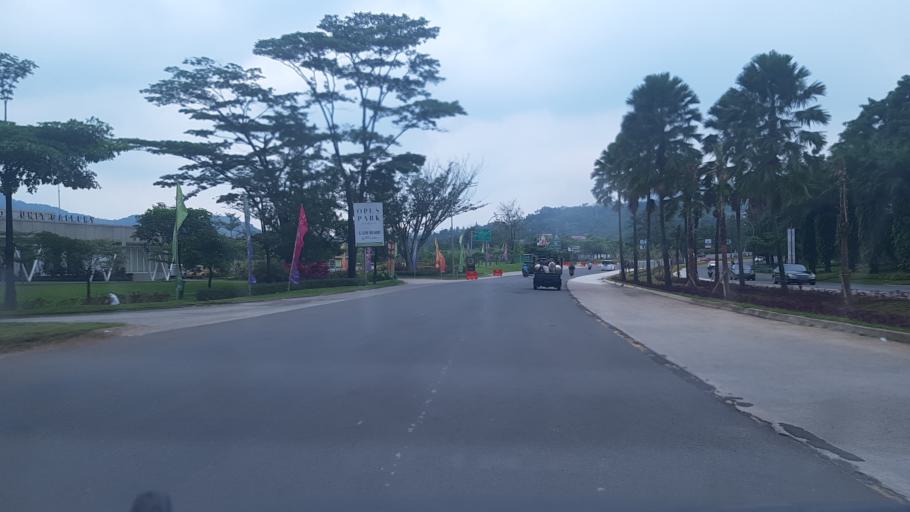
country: ID
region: West Java
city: Bogor
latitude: -6.5680
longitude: 106.8592
